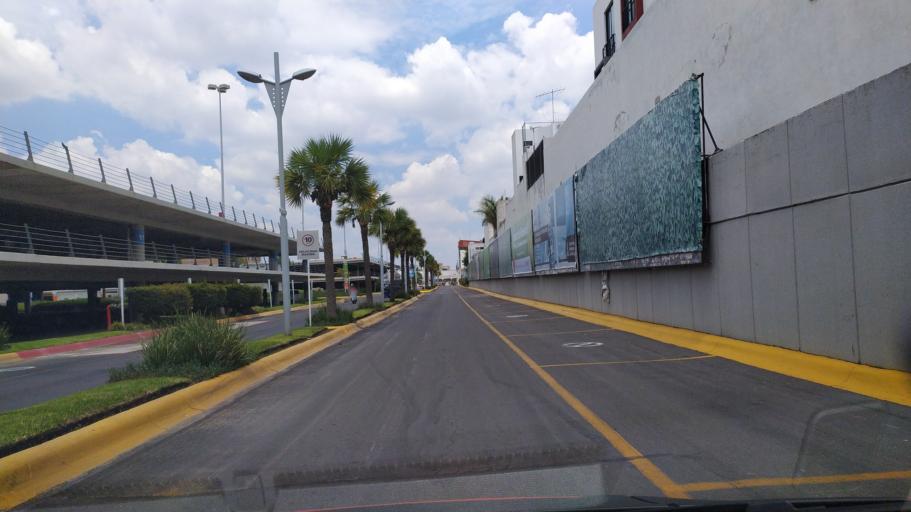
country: MX
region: Jalisco
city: Guadalajara
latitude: 20.6758
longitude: -103.4331
